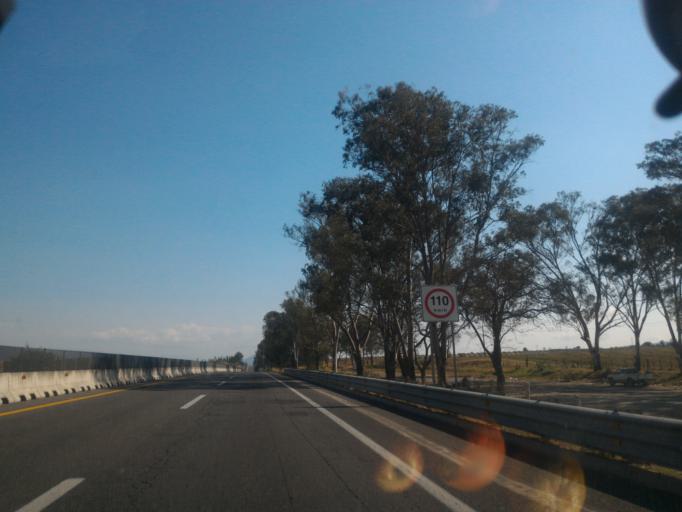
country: MX
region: Jalisco
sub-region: Zapotlan el Grande
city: Ciudad Guzman [CERESO]
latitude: 19.6279
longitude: -103.4649
